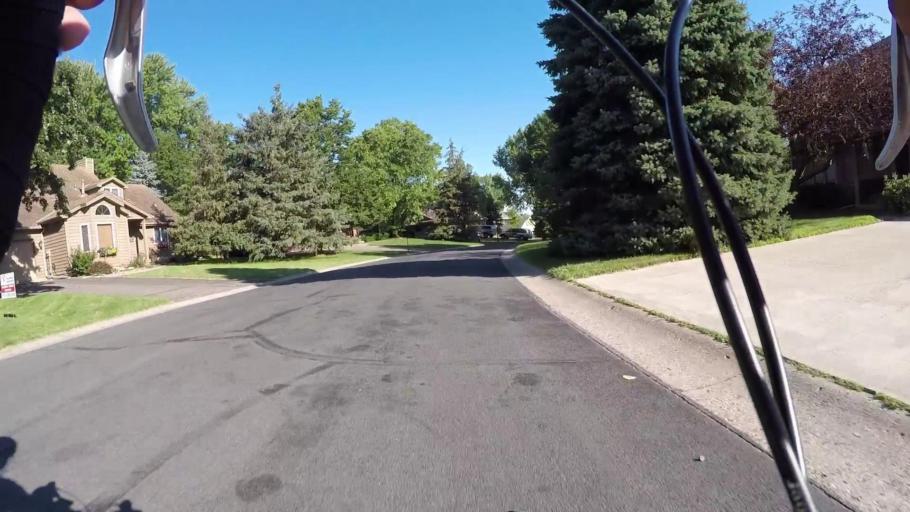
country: US
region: Minnesota
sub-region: Hennepin County
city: Minnetonka
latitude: 44.8805
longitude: -93.5021
